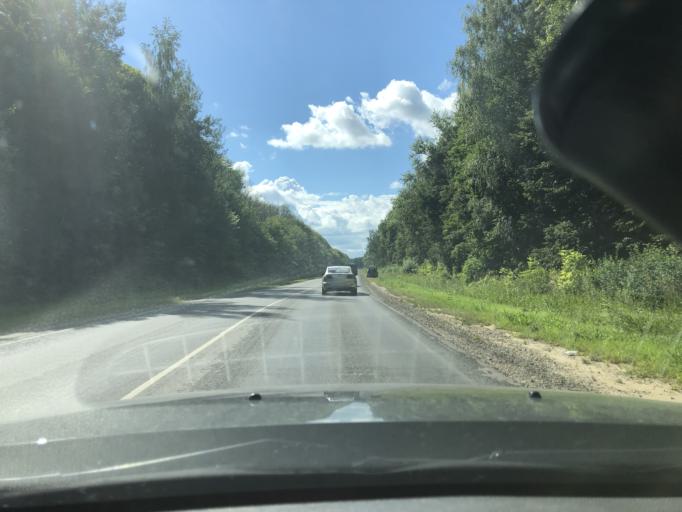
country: RU
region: Tula
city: Severo-Zadonsk
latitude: 53.9685
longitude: 38.4298
